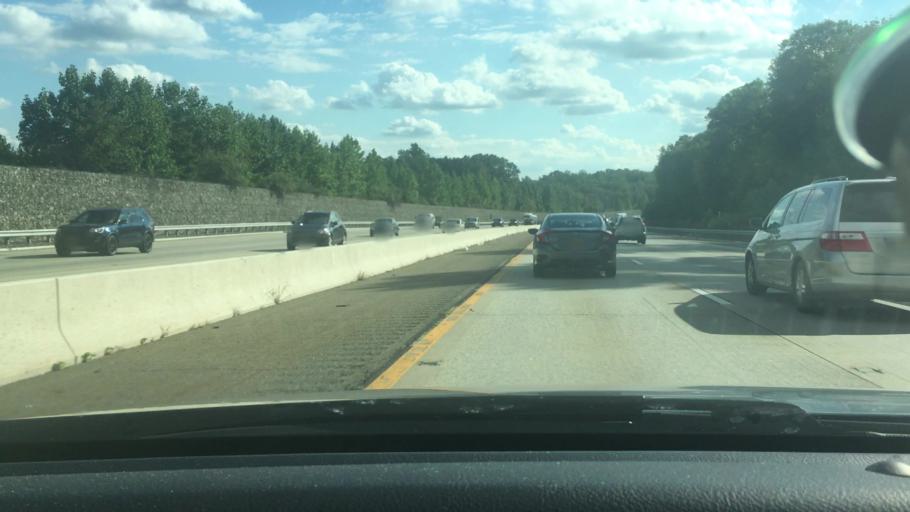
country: US
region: New Jersey
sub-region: Morris County
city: Lincoln Park
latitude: 40.9424
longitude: -74.3474
